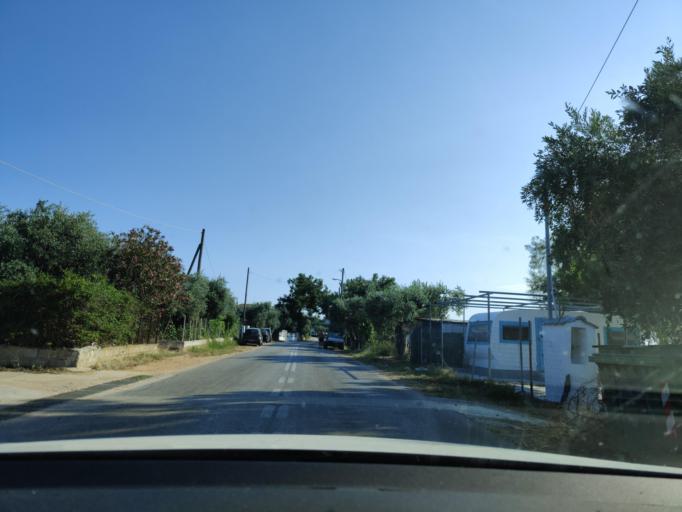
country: GR
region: East Macedonia and Thrace
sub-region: Nomos Kavalas
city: Prinos
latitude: 40.7011
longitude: 24.5287
